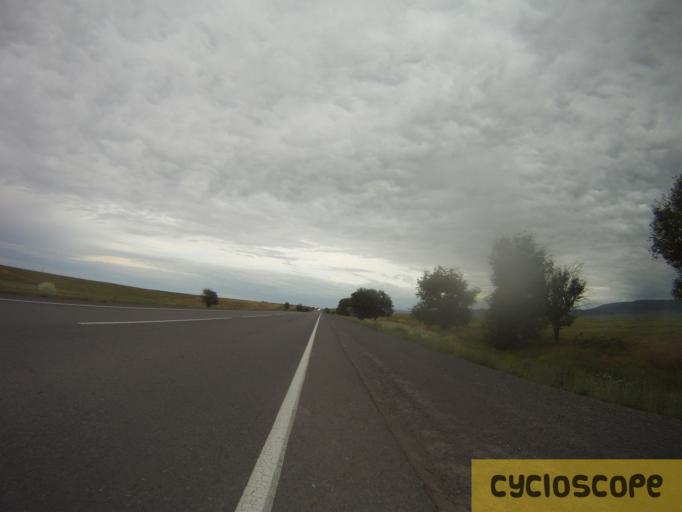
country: KG
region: Chuy
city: Tokmok
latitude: 43.3616
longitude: 75.3761
